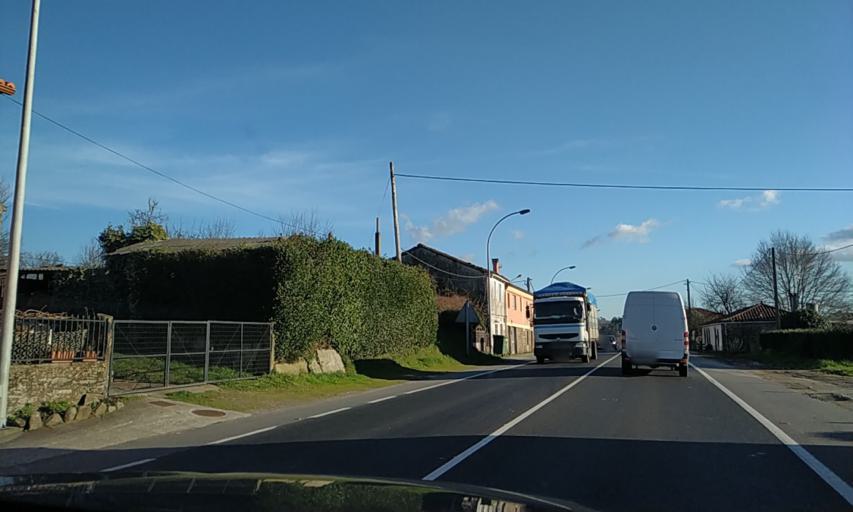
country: ES
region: Galicia
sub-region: Provincia de Pontevedra
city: Lalin
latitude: 42.6801
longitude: -8.1666
